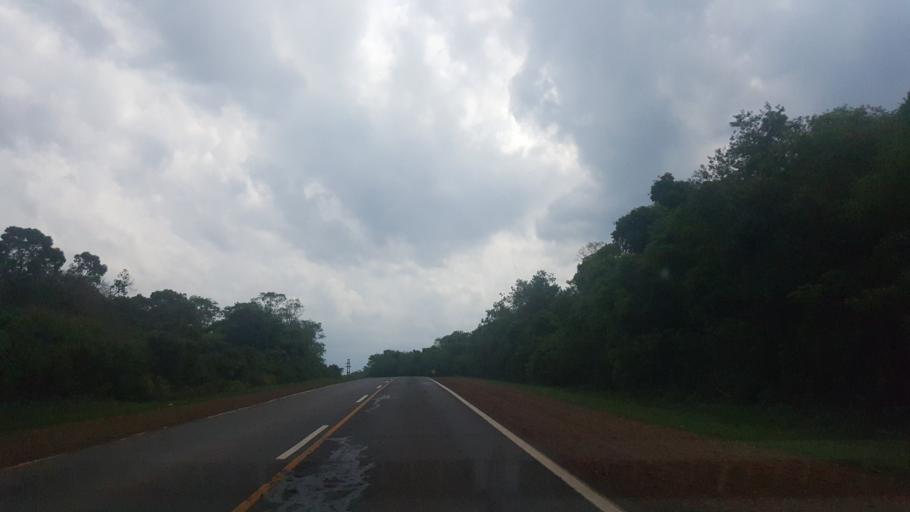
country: AR
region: Misiones
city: Santo Pipo
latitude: -27.1146
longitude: -55.3602
